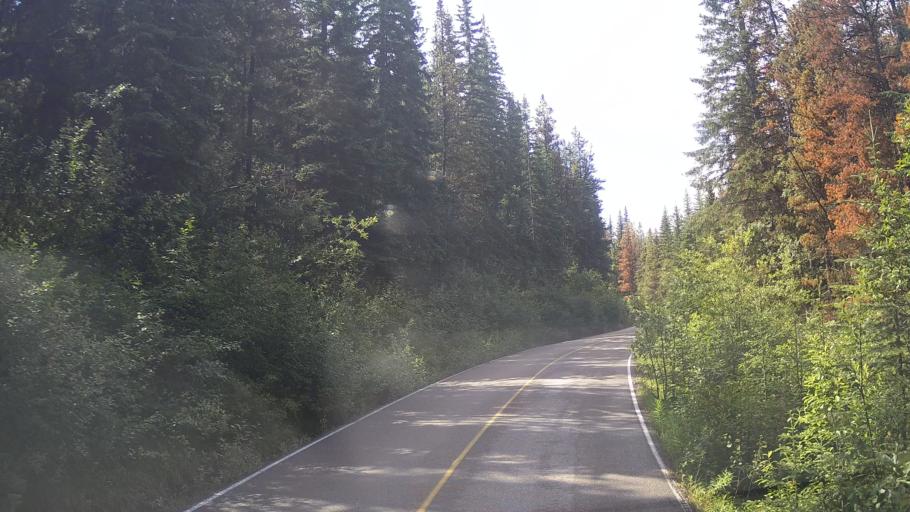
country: CA
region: Alberta
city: Jasper Park Lodge
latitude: 52.7508
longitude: -118.0456
